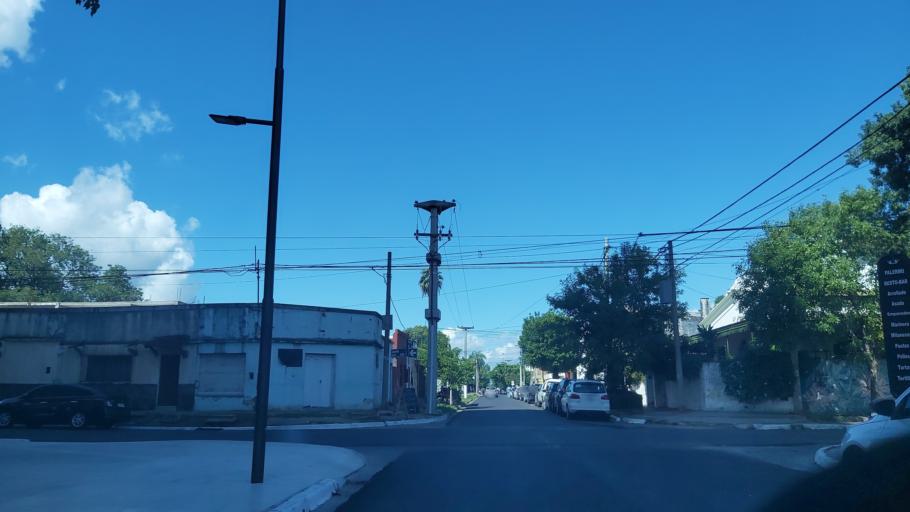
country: AR
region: Corrientes
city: Corrientes
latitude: -27.4755
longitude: -58.8470
